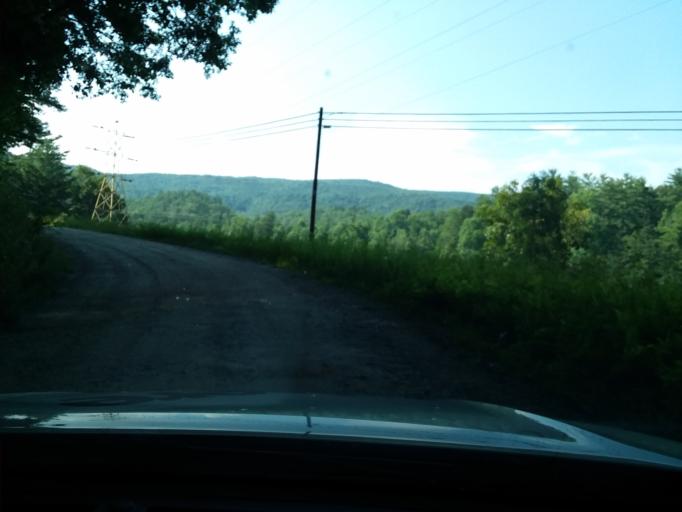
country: US
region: Georgia
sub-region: Habersham County
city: Clarkesville
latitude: 34.7533
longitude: -83.4825
